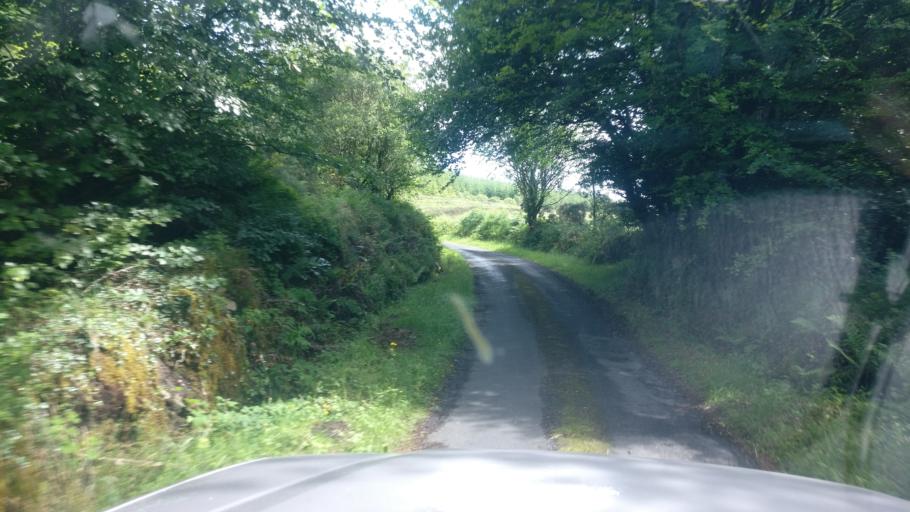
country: IE
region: Connaught
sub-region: County Galway
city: Gort
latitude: 53.0800
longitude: -8.7099
